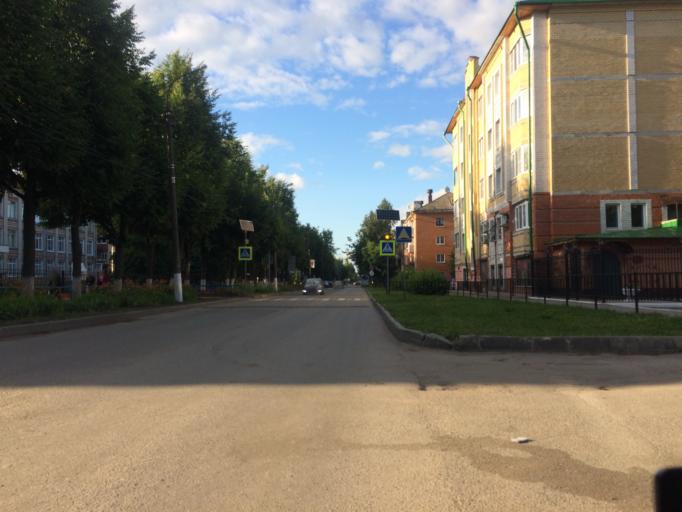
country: RU
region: Mariy-El
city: Yoshkar-Ola
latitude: 56.6351
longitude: 47.8803
